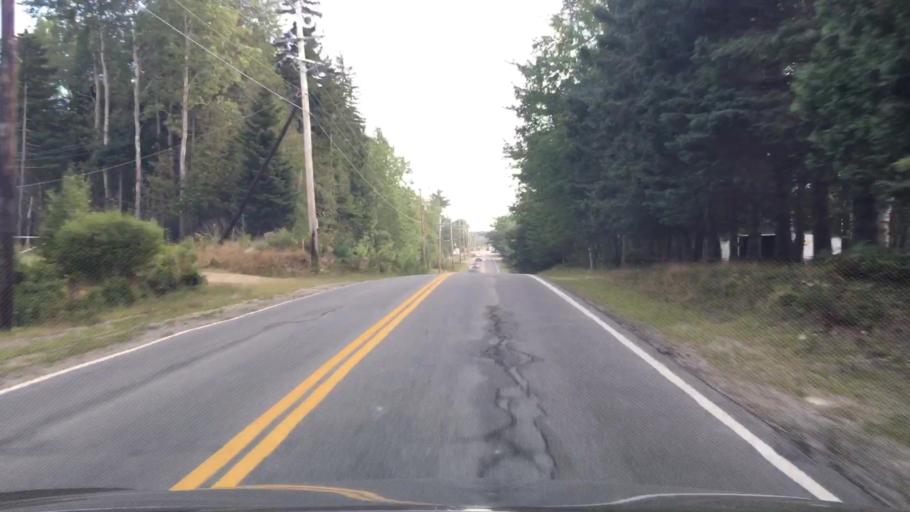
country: US
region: Maine
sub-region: Hancock County
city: Surry
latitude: 44.4346
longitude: -68.5730
